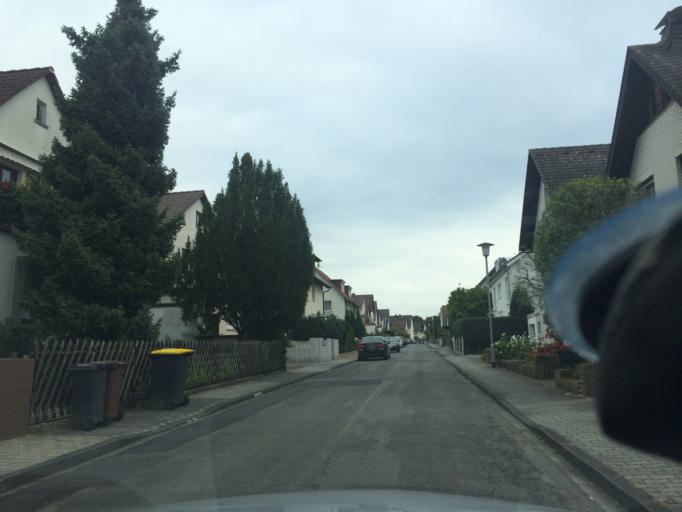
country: DE
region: Hesse
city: Morfelden-Walldorf
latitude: 49.9982
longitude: 8.5807
